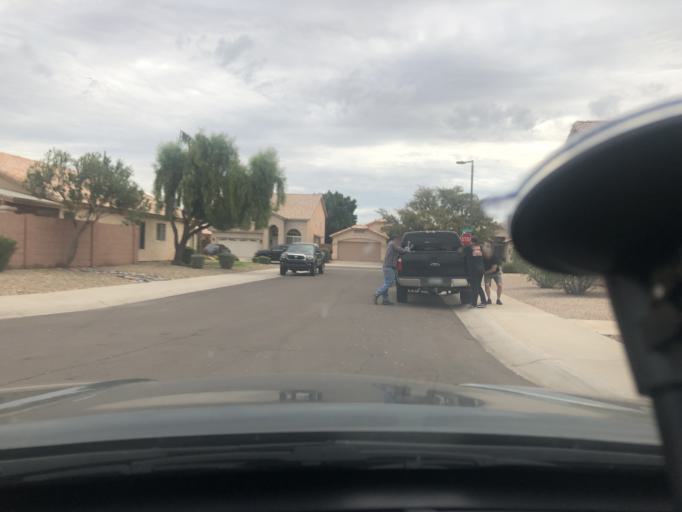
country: US
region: Arizona
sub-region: Maricopa County
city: Scottsdale
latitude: 33.4837
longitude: -111.8942
